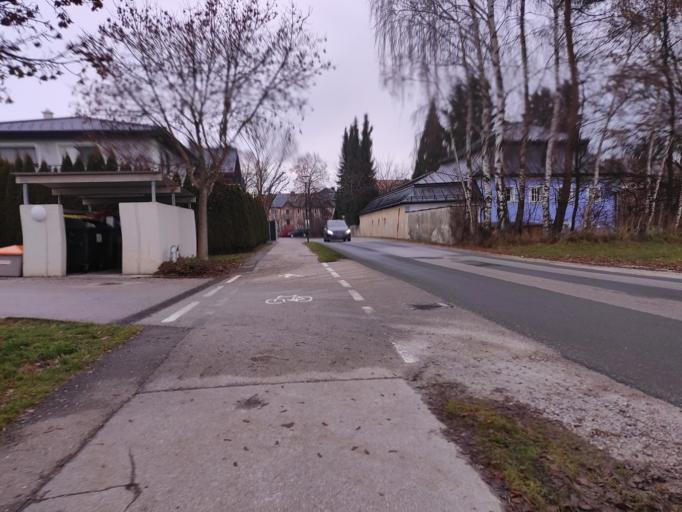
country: AT
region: Salzburg
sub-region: Politischer Bezirk Salzburg-Umgebung
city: Obertrum am See
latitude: 47.9355
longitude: 13.0760
